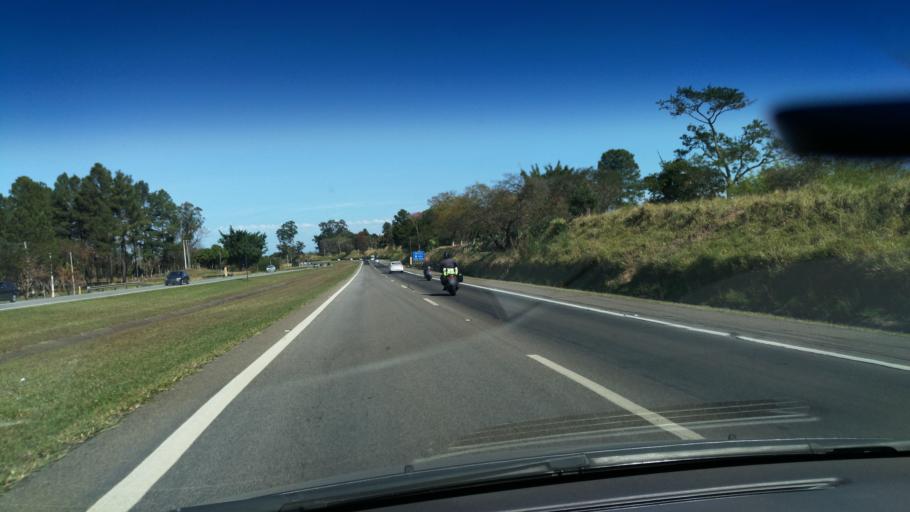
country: BR
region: Sao Paulo
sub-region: Jaguariuna
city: Jaguariuna
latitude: -22.6382
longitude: -47.0043
